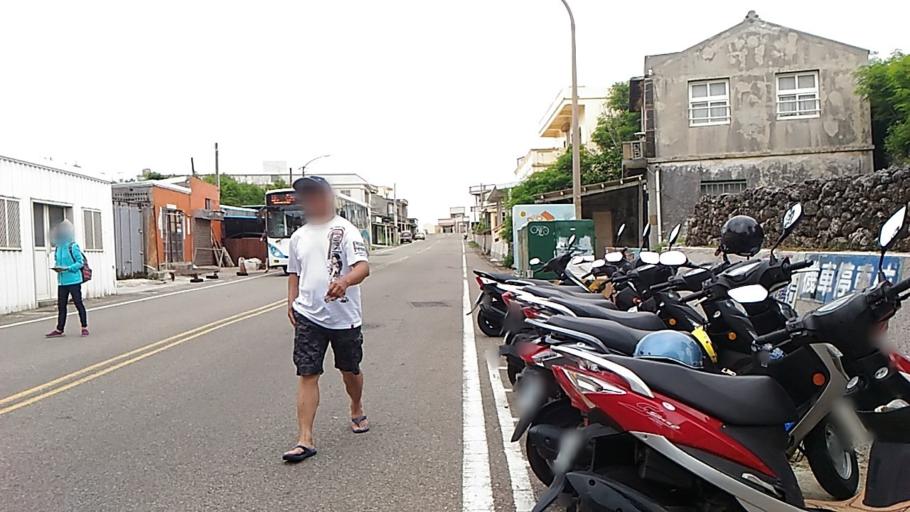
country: TW
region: Taiwan
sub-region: Penghu
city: Ma-kung
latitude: 23.6567
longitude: 119.5574
